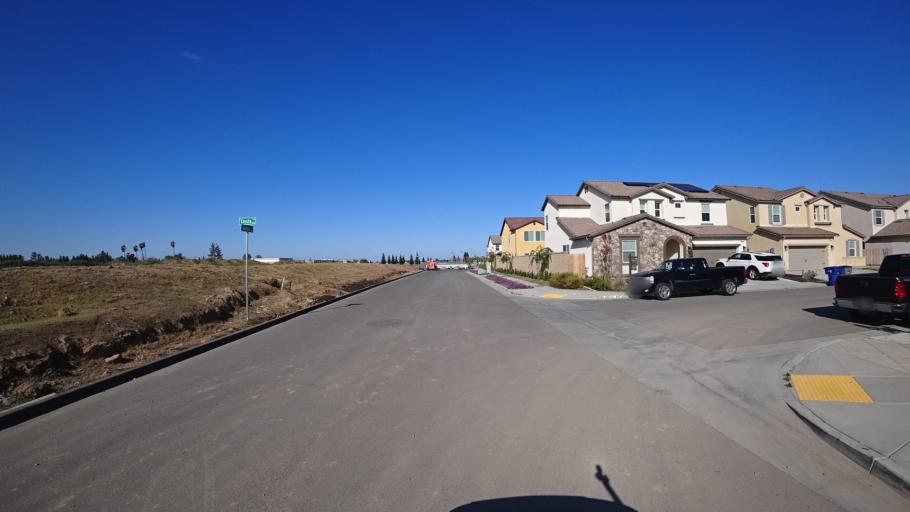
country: US
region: California
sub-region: Fresno County
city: West Park
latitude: 36.7970
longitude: -119.9043
